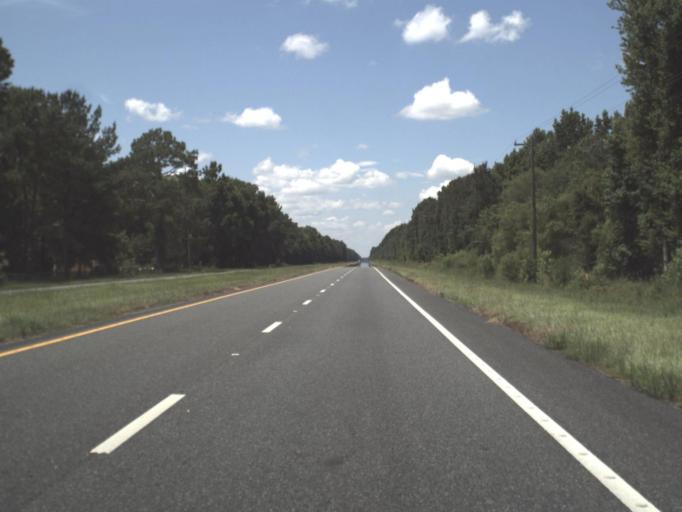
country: US
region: Florida
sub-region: Taylor County
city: Perry
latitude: 30.2675
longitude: -83.7156
